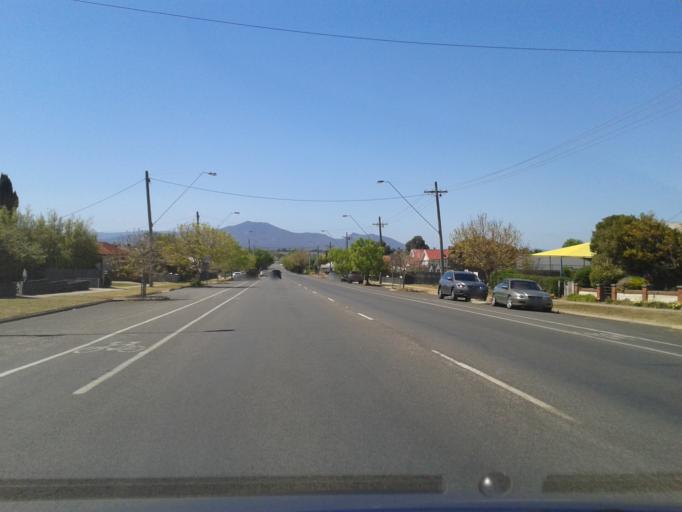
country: AU
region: Victoria
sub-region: Ararat
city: Ararat
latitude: -37.2845
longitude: 142.9393
